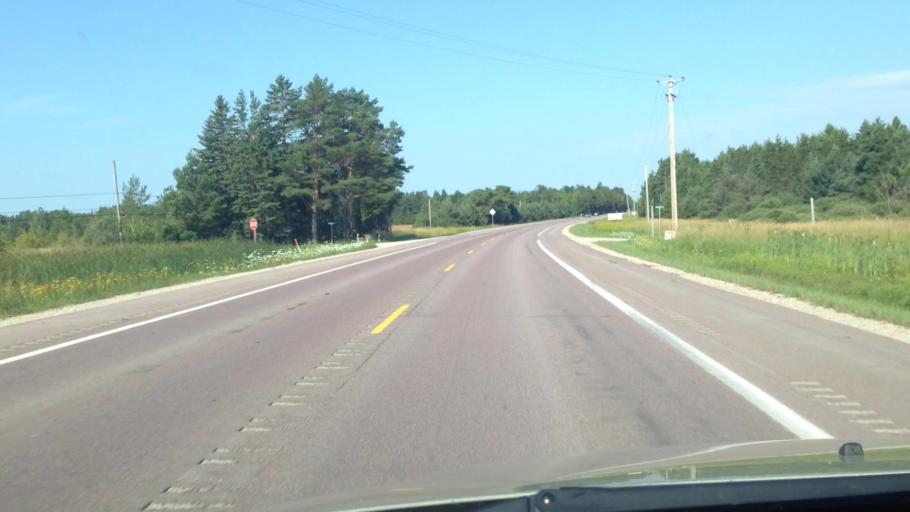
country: US
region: Michigan
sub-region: Schoolcraft County
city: Manistique
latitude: 45.9873
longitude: -86.1047
